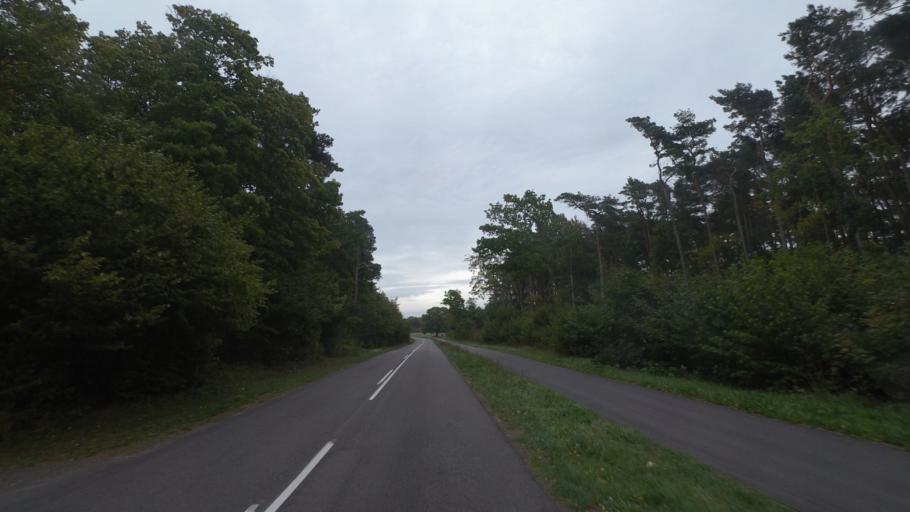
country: DK
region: Capital Region
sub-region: Bornholm Kommune
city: Nexo
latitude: 55.0027
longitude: 15.0262
